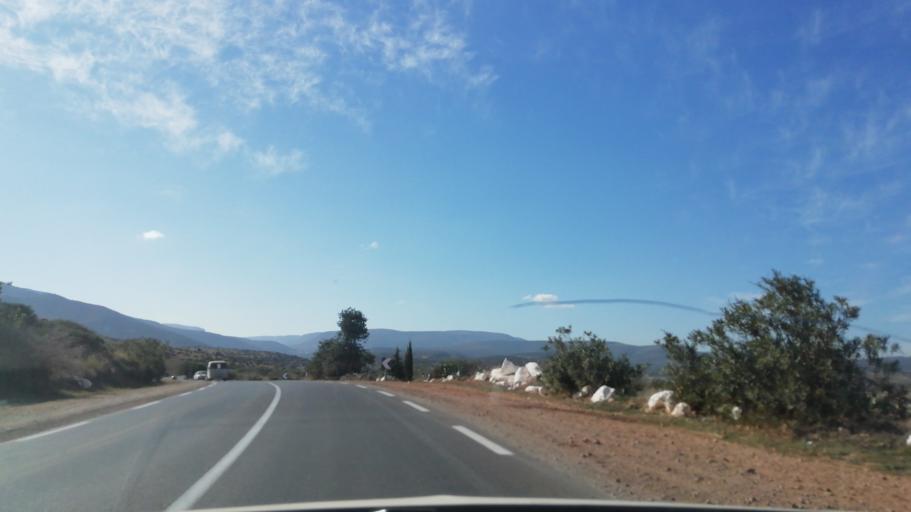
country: DZ
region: Tlemcen
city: Ouled Mimoun
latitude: 34.8753
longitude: -1.1207
